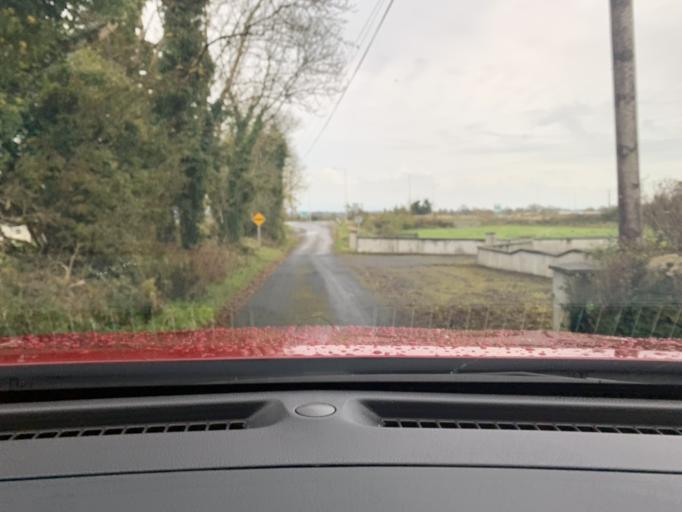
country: IE
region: Connaught
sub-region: Roscommon
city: Ballaghaderreen
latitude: 53.9140
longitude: -8.5542
